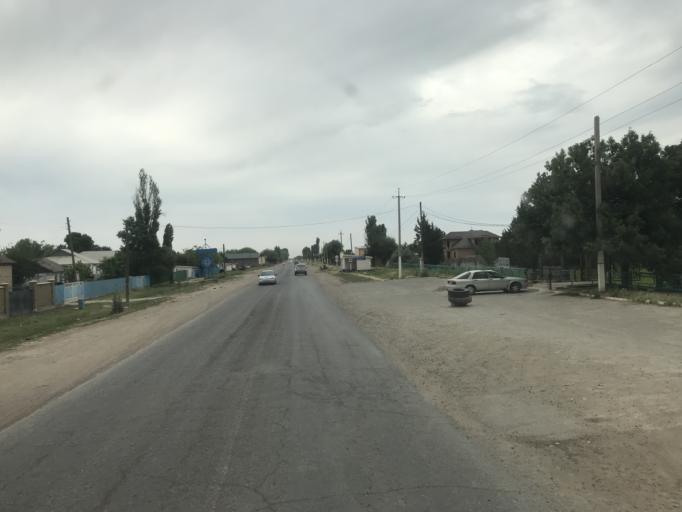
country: KZ
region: Ongtustik Qazaqstan
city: Asykata
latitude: 40.9018
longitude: 68.3580
